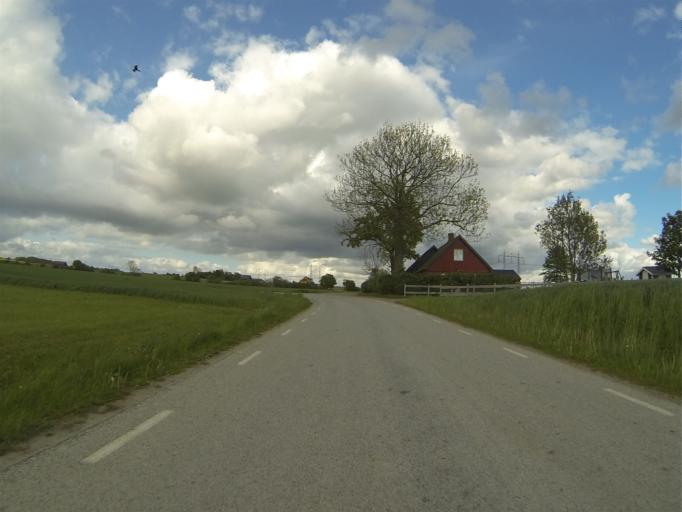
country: SE
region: Skane
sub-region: Staffanstorps Kommun
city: Staffanstorp
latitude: 55.6842
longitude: 13.2861
